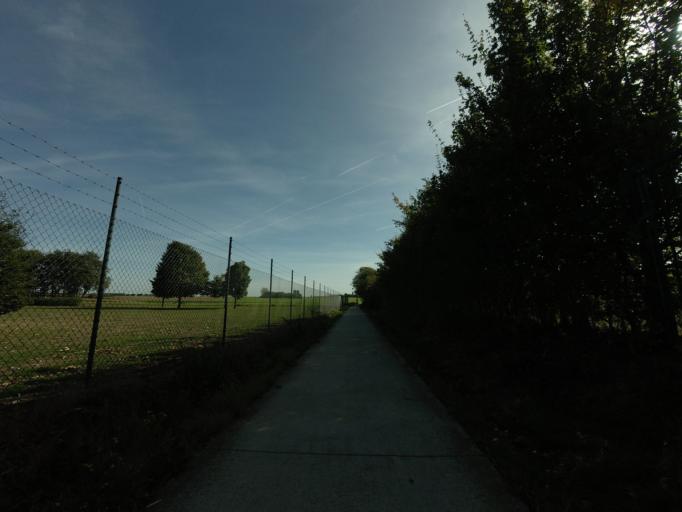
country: BE
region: Flanders
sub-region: Provincie Vlaams-Brabant
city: Diegem
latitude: 50.8779
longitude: 4.4378
